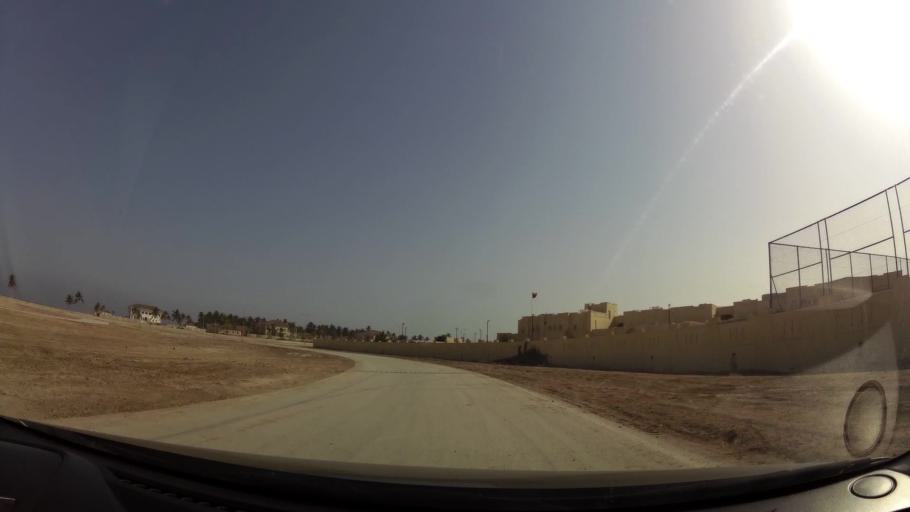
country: OM
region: Zufar
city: Salalah
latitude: 16.9957
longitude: 54.0498
